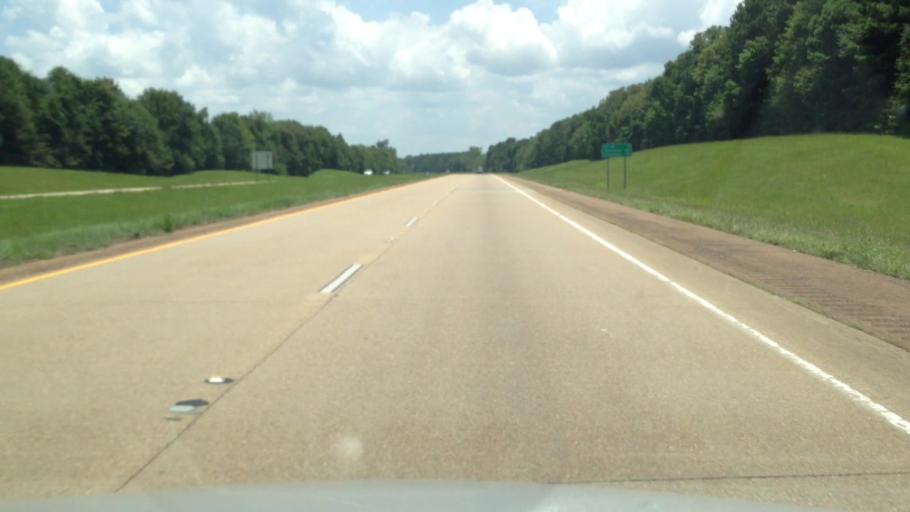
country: US
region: Louisiana
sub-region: Rapides Parish
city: Woodworth
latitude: 31.1507
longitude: -92.4536
